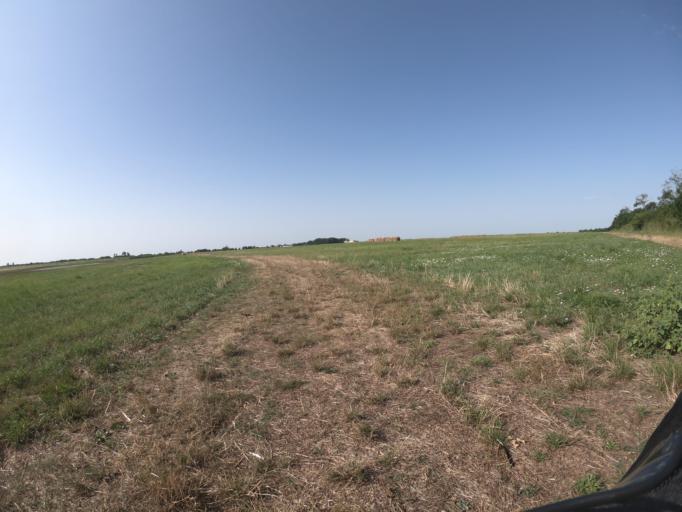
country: HU
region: Hajdu-Bihar
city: Egyek
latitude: 47.5810
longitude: 20.9470
